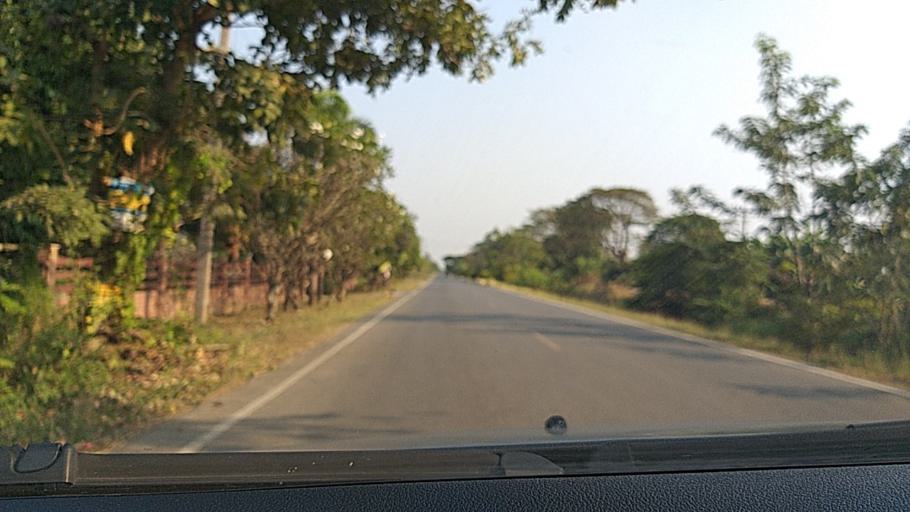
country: TH
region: Sing Buri
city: Sing Buri
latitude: 14.8367
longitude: 100.3963
